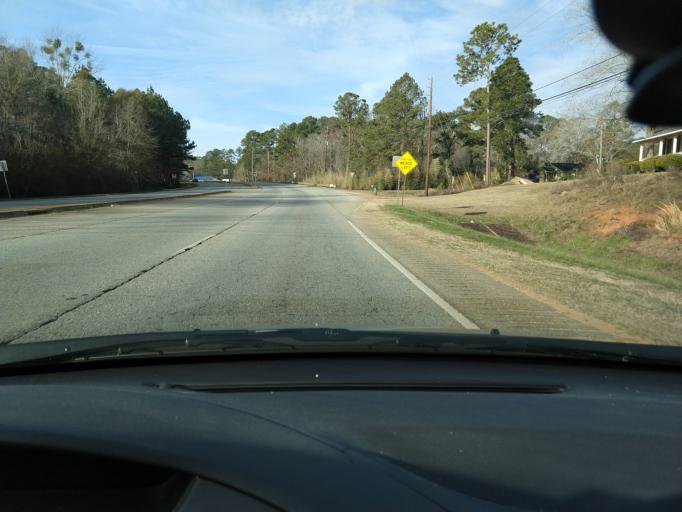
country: US
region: Georgia
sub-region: Sumter County
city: Americus
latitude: 32.0616
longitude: -84.2656
